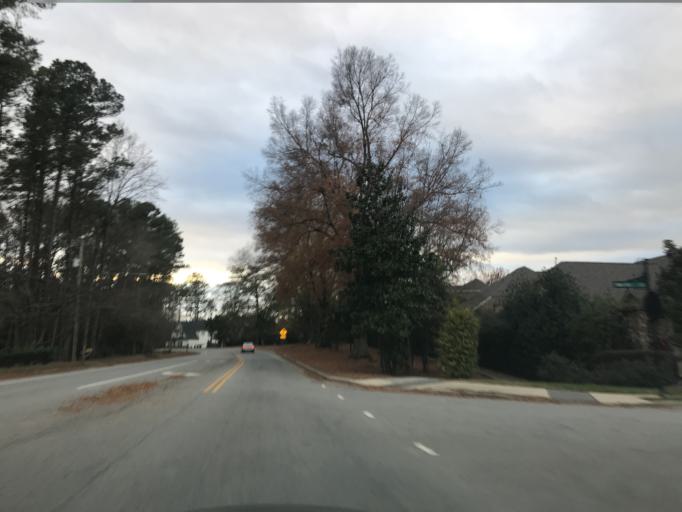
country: US
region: North Carolina
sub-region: Wake County
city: West Raleigh
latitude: 35.8299
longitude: -78.6882
